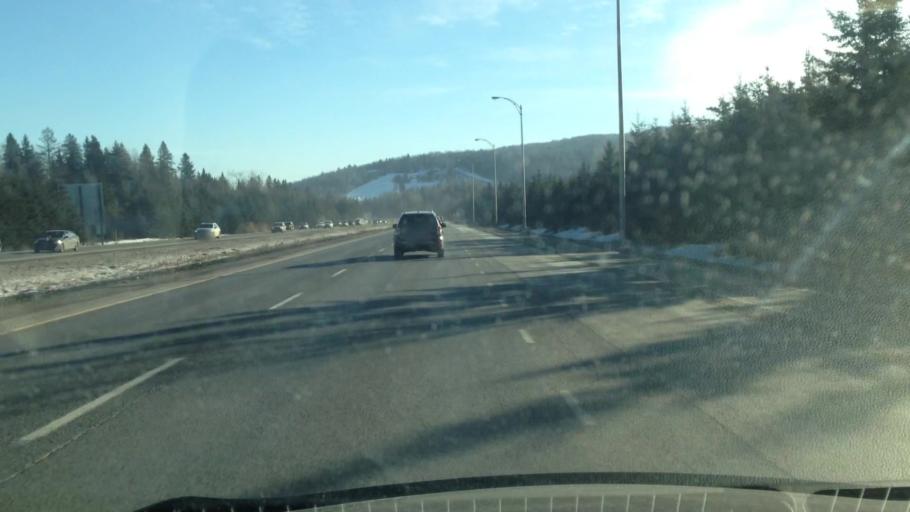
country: CA
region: Quebec
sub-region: Laurentides
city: Saint-Sauveur
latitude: 45.8883
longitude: -74.1384
